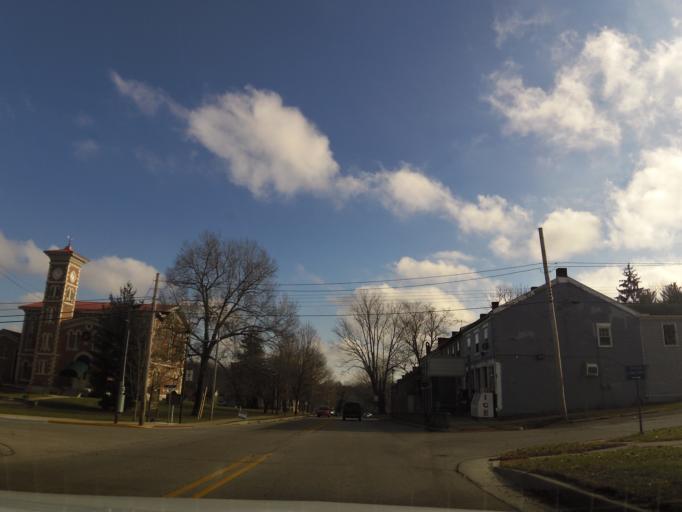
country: US
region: Indiana
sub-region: Jennings County
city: North Vernon
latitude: 38.9846
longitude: -85.6097
